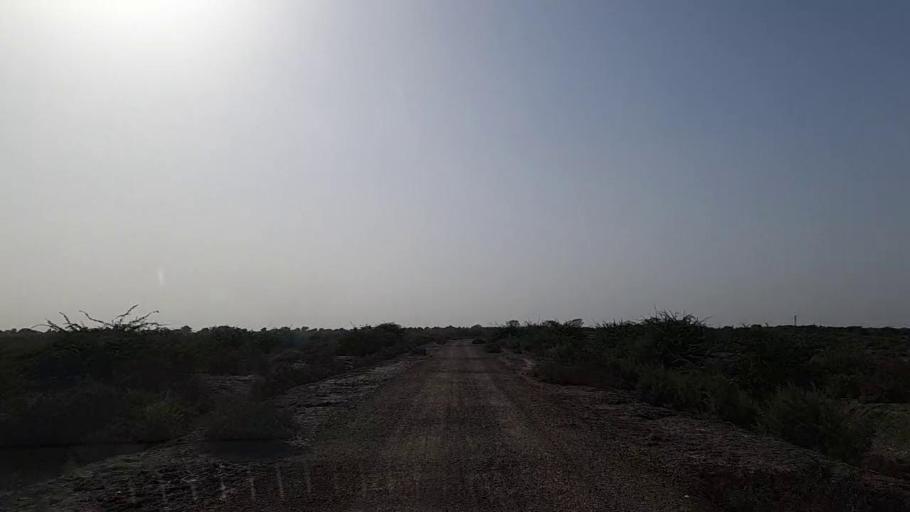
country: PK
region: Sindh
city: Jati
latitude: 24.2858
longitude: 68.2135
